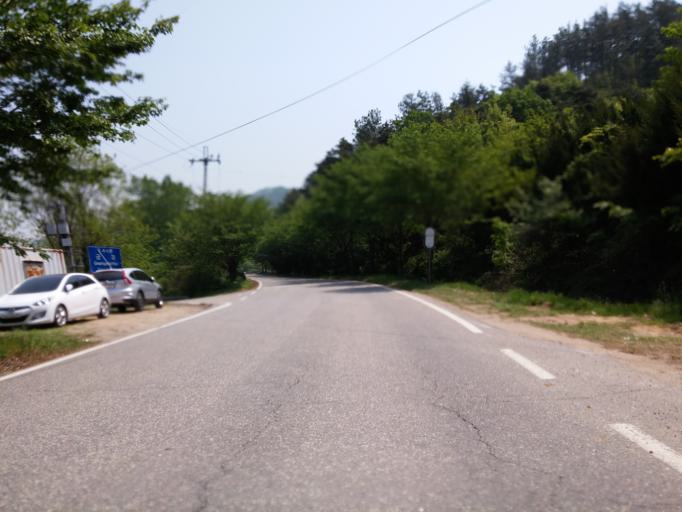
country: KR
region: Daejeon
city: Sintansin
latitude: 36.4328
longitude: 127.5475
